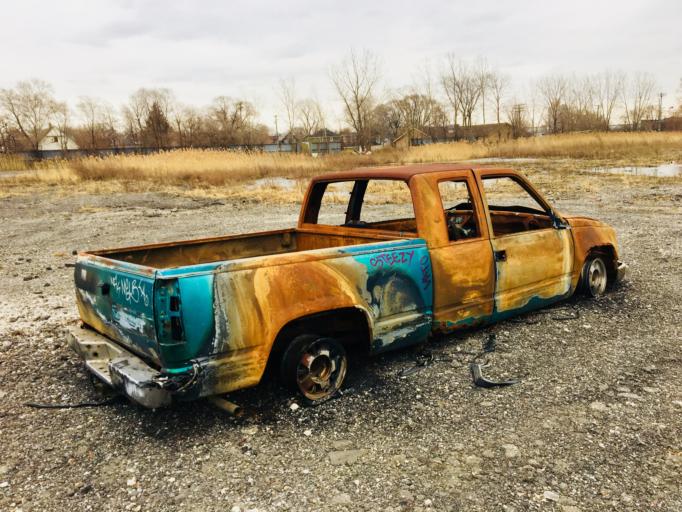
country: US
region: Michigan
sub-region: Wayne County
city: River Rouge
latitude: 42.2962
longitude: -83.1135
